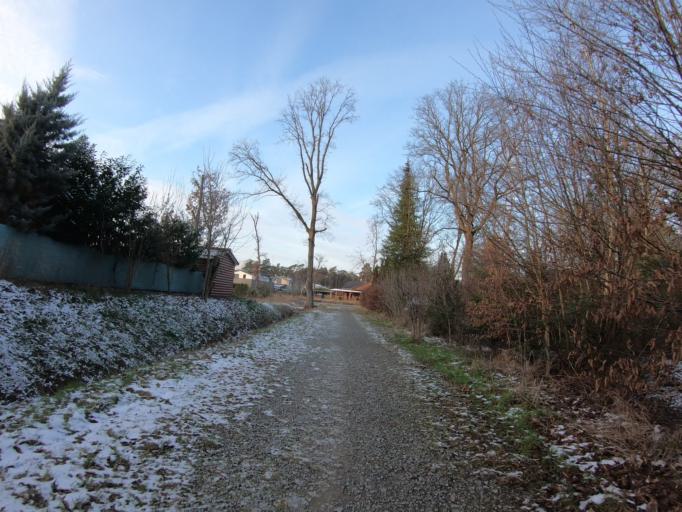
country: DE
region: Lower Saxony
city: Isenbuttel
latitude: 52.4542
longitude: 10.6069
